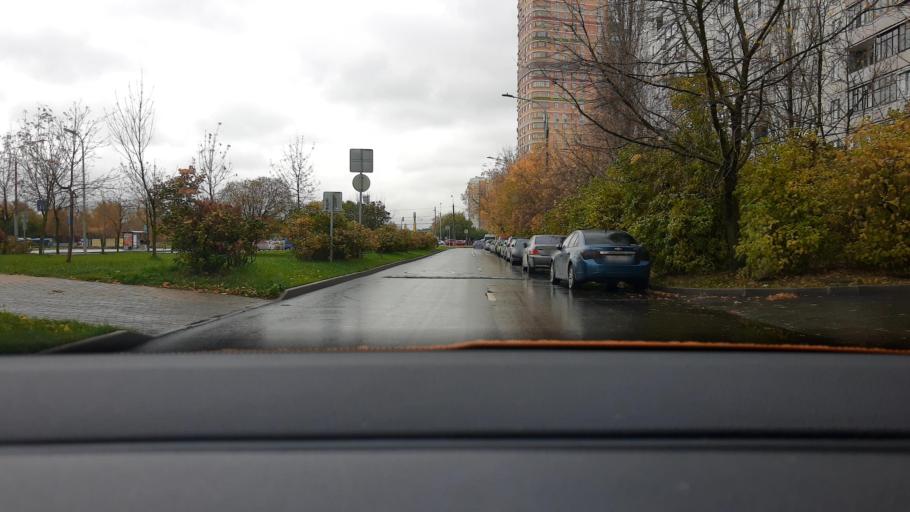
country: RU
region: Moscow
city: Strogino
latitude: 55.8064
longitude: 37.4166
